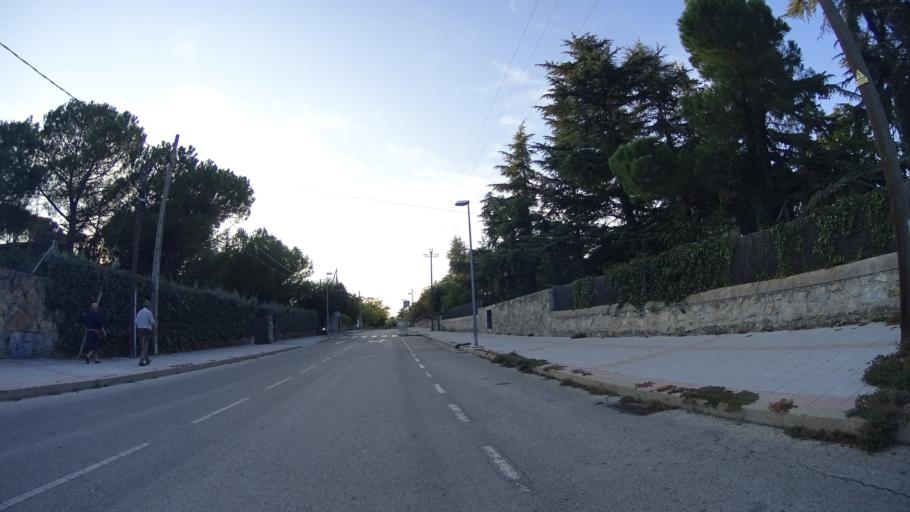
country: ES
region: Madrid
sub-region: Provincia de Madrid
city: Galapagar
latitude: 40.5758
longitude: -3.9921
